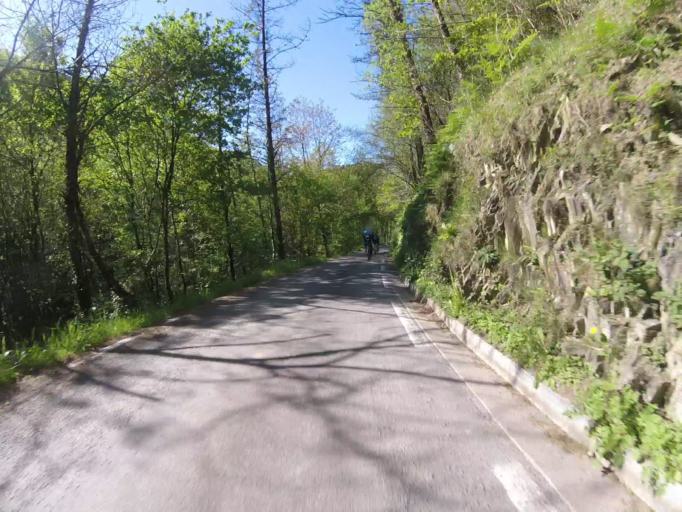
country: ES
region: Basque Country
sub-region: Provincia de Guipuzcoa
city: Errezil
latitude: 43.1806
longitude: -2.2031
